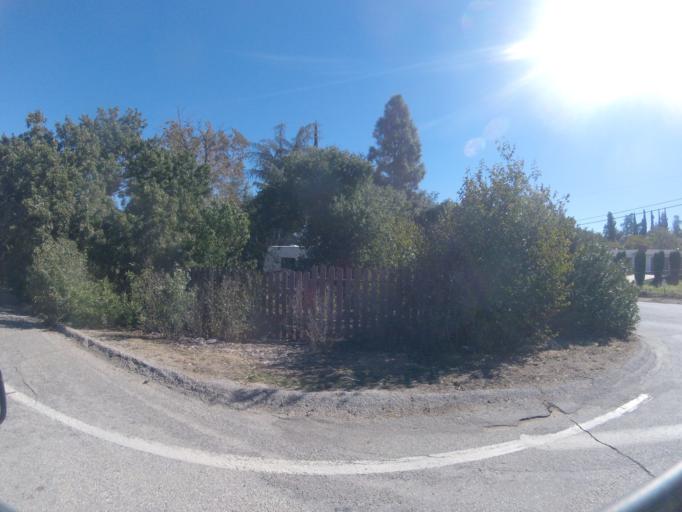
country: US
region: California
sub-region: San Bernardino County
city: Mentone
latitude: 34.0229
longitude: -117.1163
